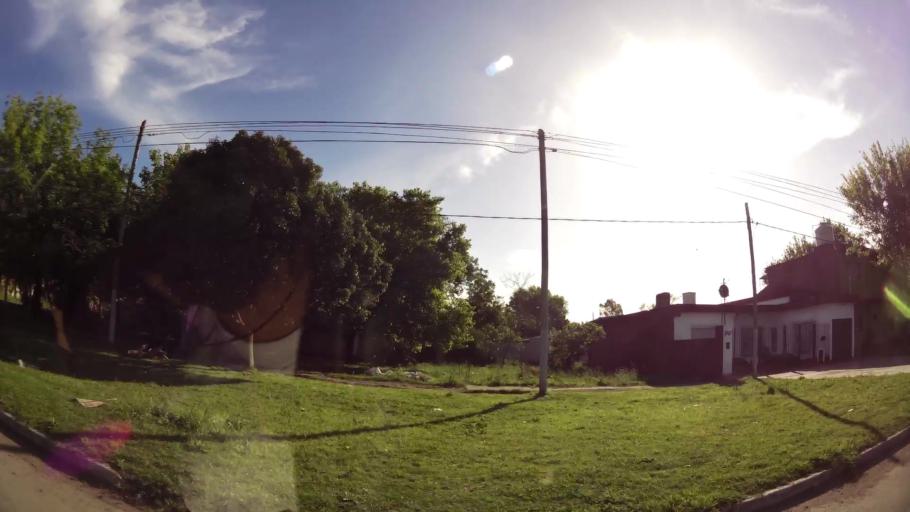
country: AR
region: Buenos Aires
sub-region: Partido de Quilmes
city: Quilmes
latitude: -34.7932
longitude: -58.2153
